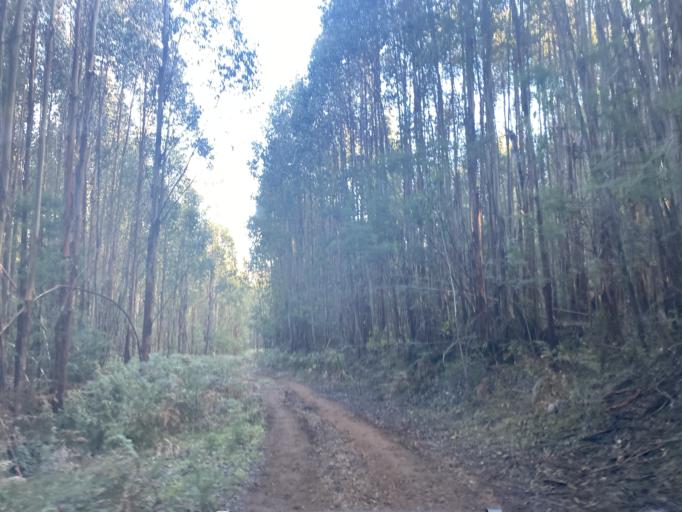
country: AU
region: Victoria
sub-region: Yarra Ranges
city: Healesville
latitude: -37.4730
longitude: 145.5775
